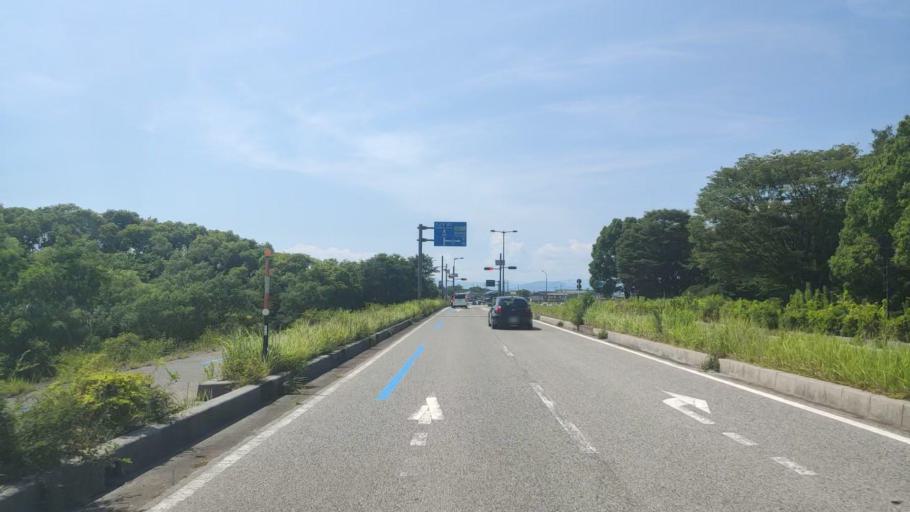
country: JP
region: Shiga Prefecture
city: Nagahama
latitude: 35.3850
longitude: 136.2479
